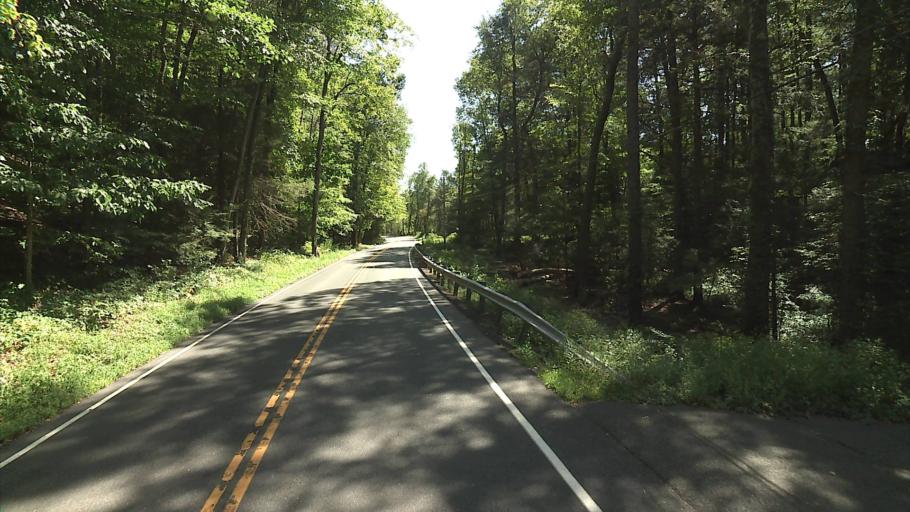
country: US
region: Connecticut
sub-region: New Haven County
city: Oxford
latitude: 41.4500
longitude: -73.1628
